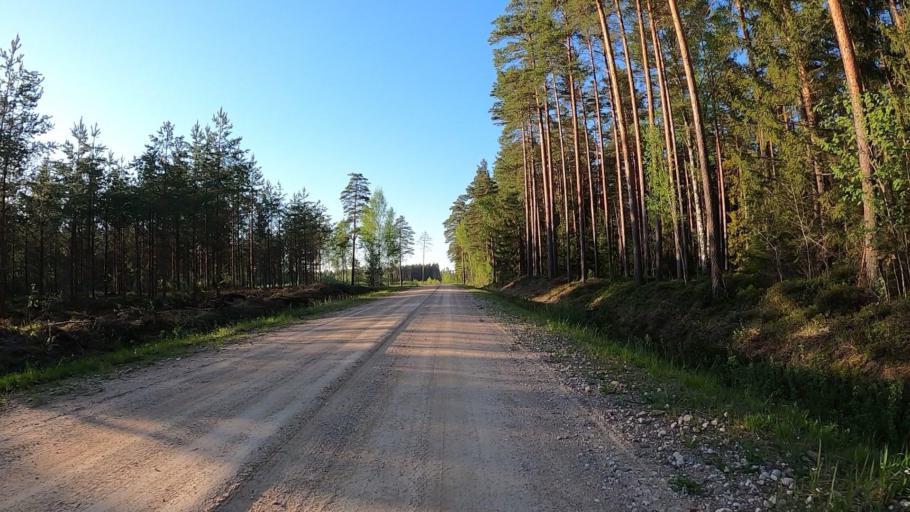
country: LV
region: Kekava
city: Kekava
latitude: 56.7671
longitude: 24.2227
